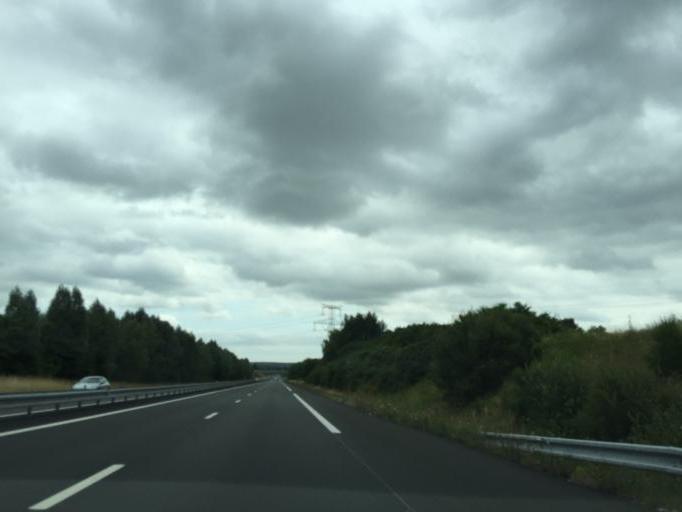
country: FR
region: Pays de la Loire
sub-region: Departement de la Sarthe
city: Ecommoy
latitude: 47.8284
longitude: 0.3064
